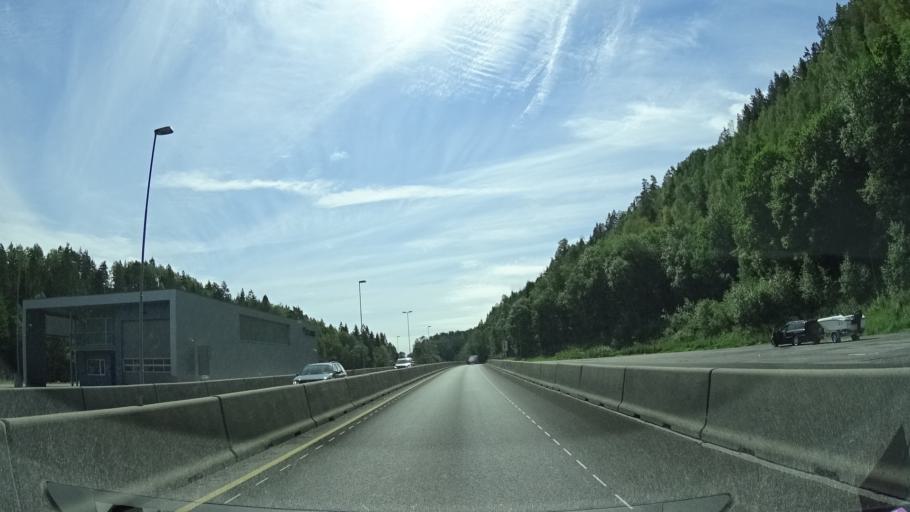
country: NO
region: Telemark
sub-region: Bamble
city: Langesund
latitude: 59.1024
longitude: 9.7677
